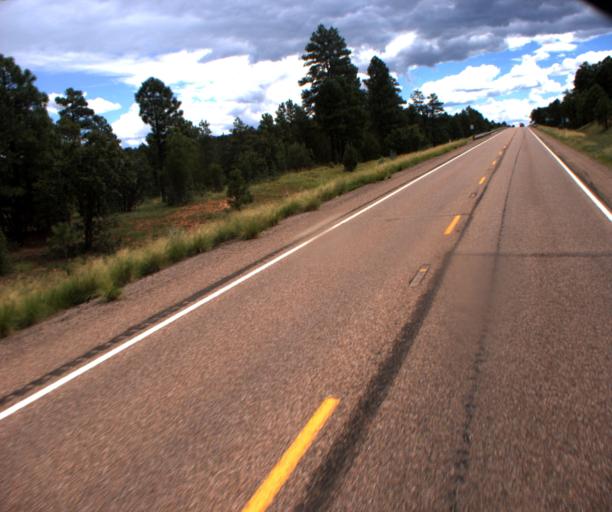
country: US
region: Arizona
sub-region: Navajo County
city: Linden
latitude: 34.3035
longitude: -110.2028
